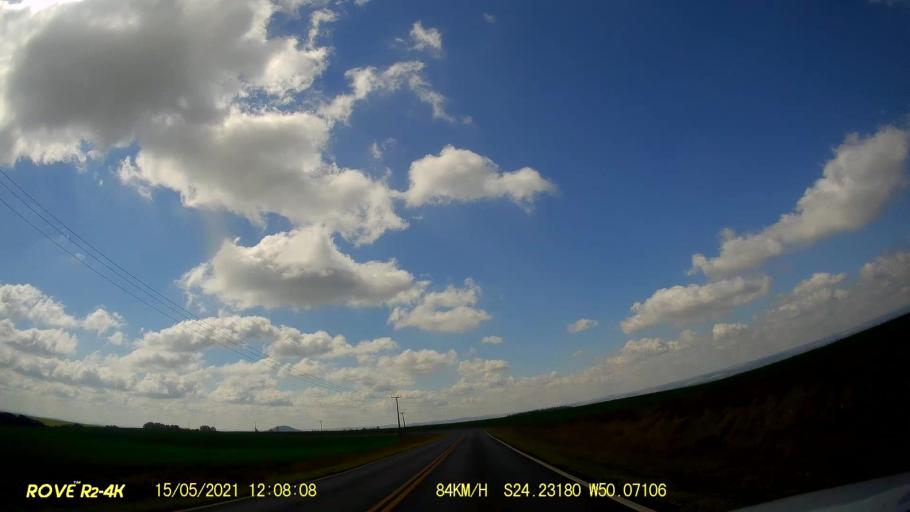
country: BR
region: Parana
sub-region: Pirai Do Sul
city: Pirai do Sul
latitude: -24.2318
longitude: -50.0710
